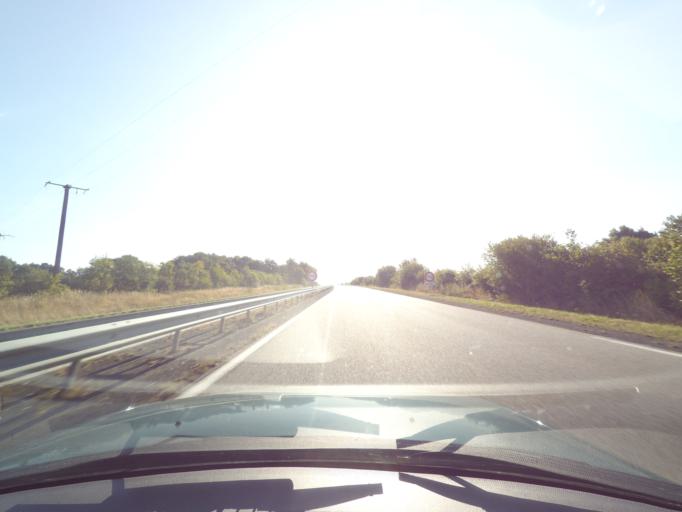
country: FR
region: Poitou-Charentes
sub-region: Departement des Deux-Sevres
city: La Peyratte
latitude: 46.6520
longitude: -0.1303
